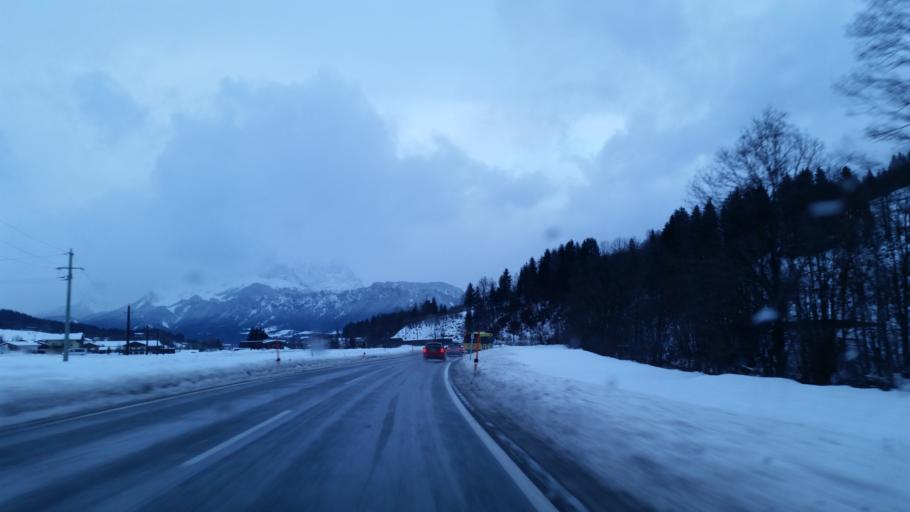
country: AT
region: Tyrol
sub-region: Politischer Bezirk Kitzbuhel
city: Sankt Johann in Tirol
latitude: 47.5011
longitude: 12.4855
